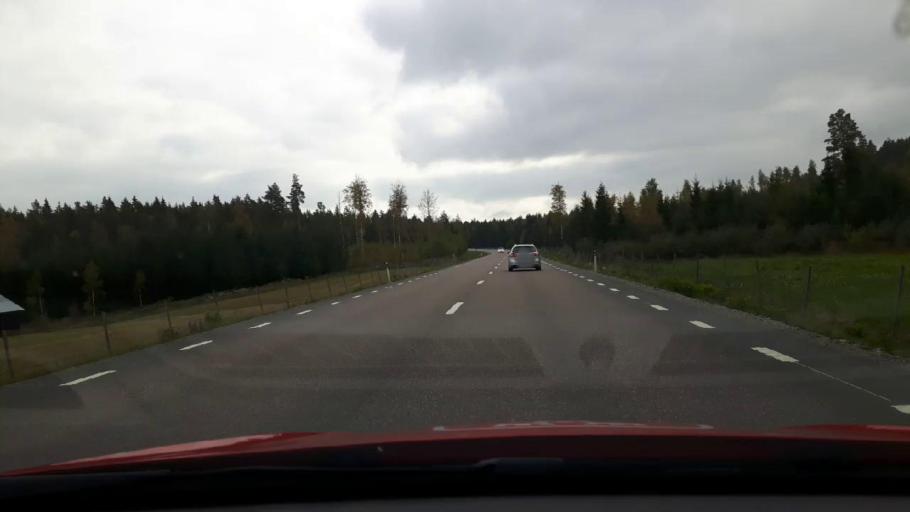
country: SE
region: Gaevleborg
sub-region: Bollnas Kommun
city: Bollnas
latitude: 61.3035
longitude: 16.4674
